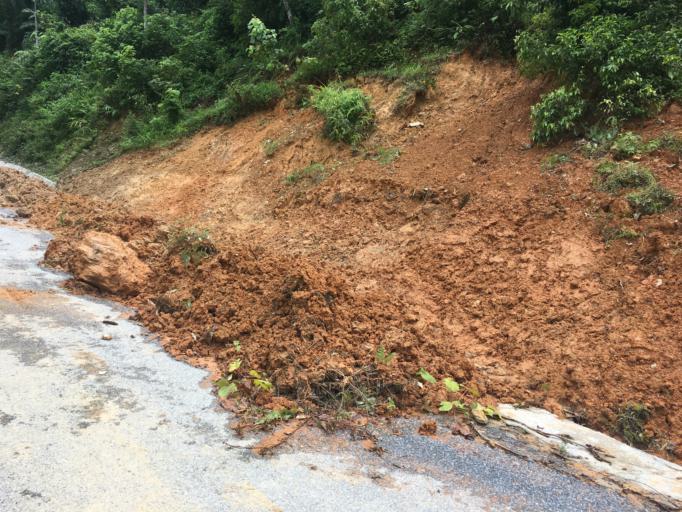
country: VN
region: Ha Giang
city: Thi Tran Tam Son
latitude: 22.9932
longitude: 105.0675
